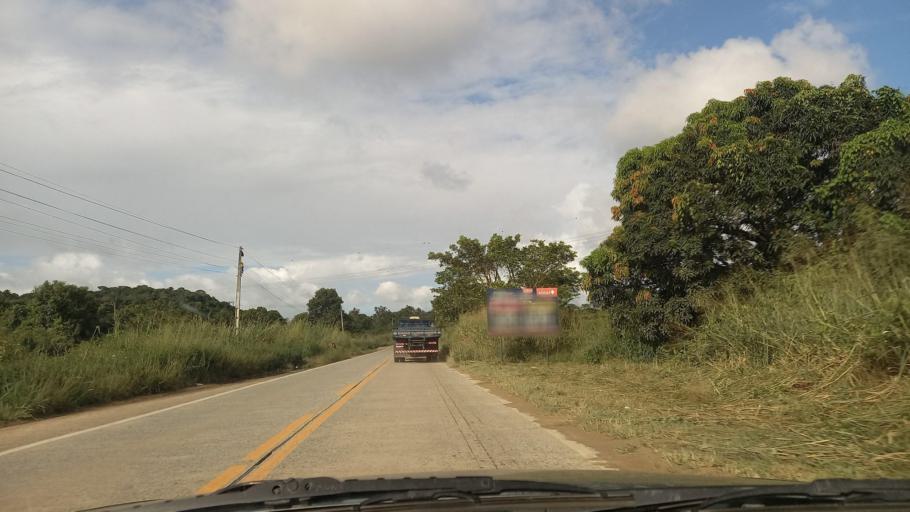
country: BR
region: Pernambuco
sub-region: Palmares
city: Palmares
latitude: -8.6910
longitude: -35.6138
